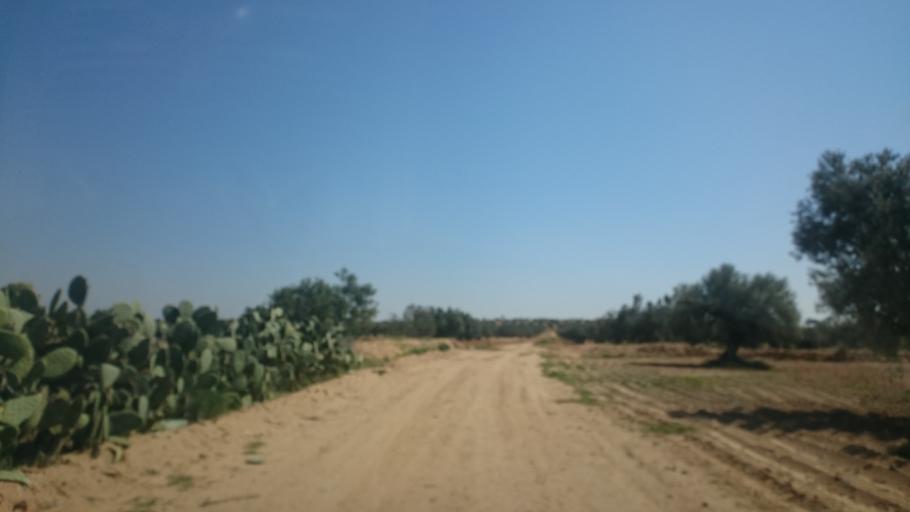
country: TN
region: Safaqis
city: Sfax
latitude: 34.7914
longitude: 10.5456
